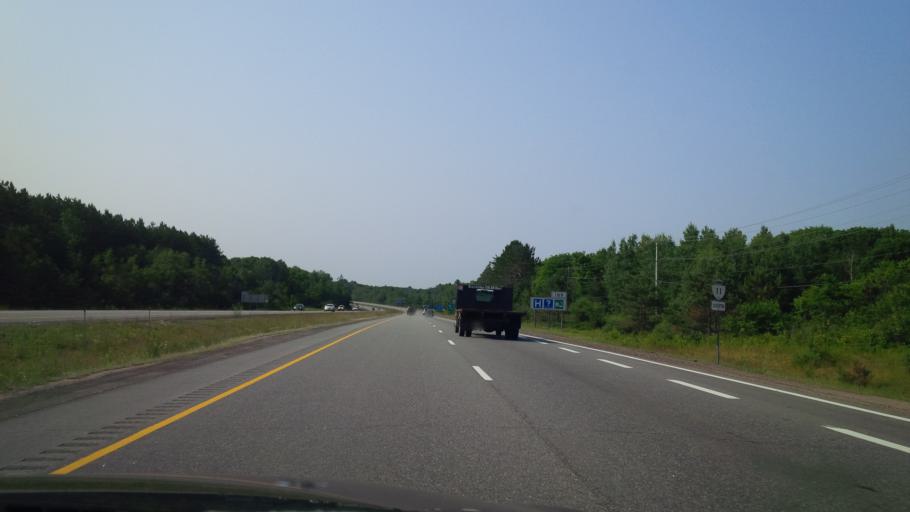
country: CA
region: Ontario
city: Bracebridge
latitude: 45.0696
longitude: -79.2972
